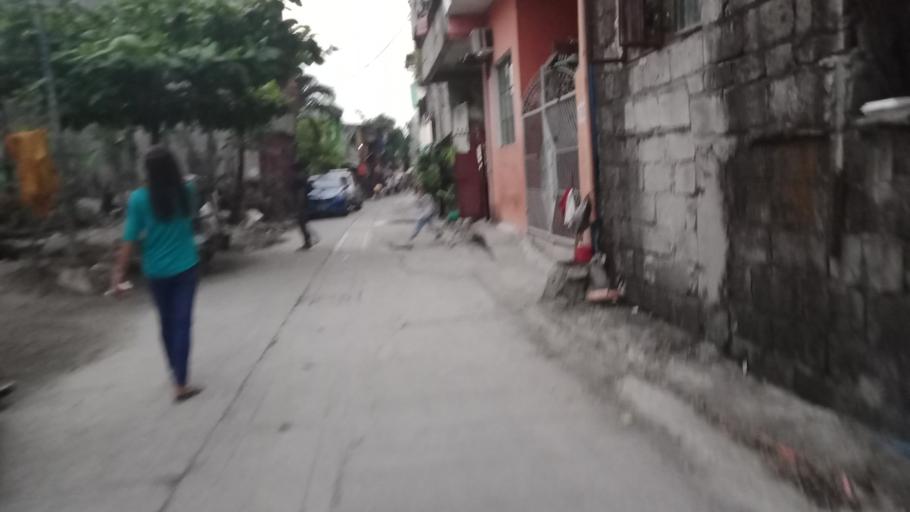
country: PH
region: Calabarzon
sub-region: Province of Rizal
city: Pateros
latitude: 14.5442
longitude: 121.1008
